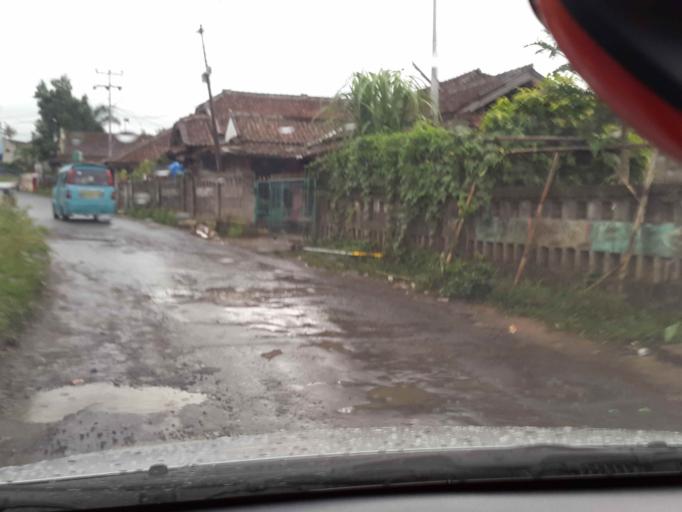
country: ID
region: West Java
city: Sukabumi
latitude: -6.8994
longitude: 106.8661
